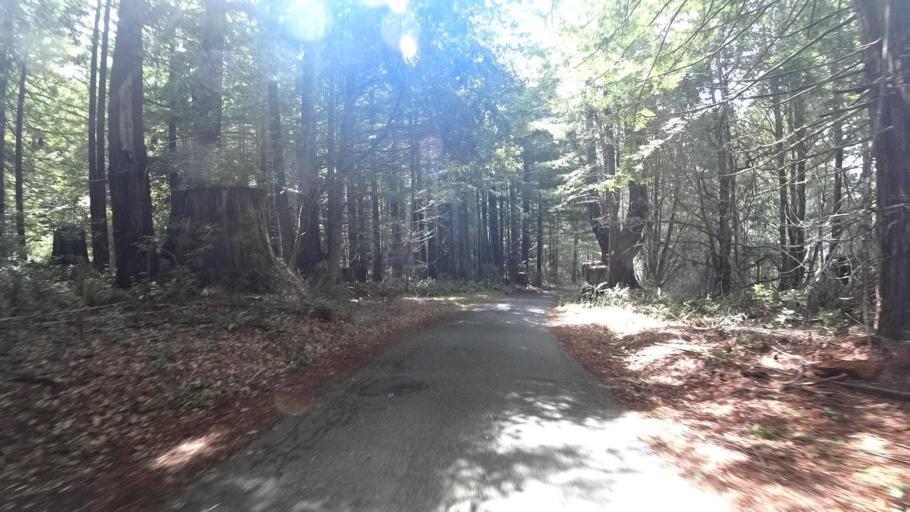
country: US
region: California
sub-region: Humboldt County
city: Blue Lake
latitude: 40.7826
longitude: -123.9625
